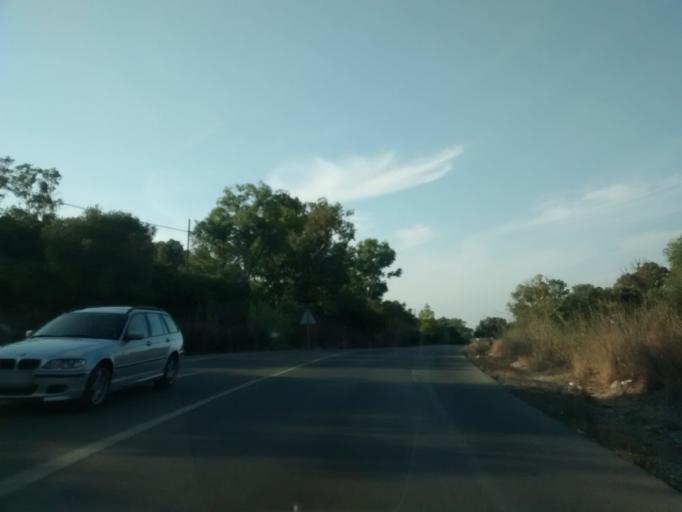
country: ES
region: Andalusia
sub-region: Provincia de Cadiz
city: Vejer de la Frontera
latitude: 36.2210
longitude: -5.9486
